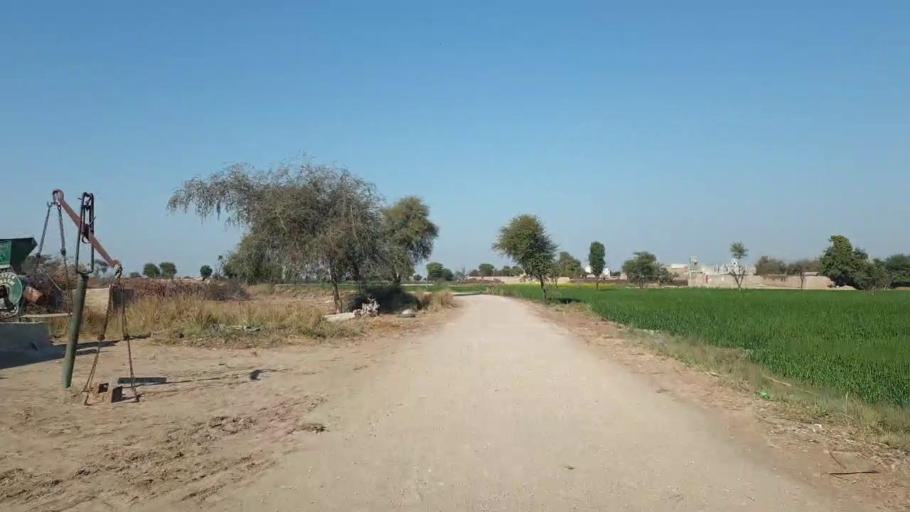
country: PK
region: Sindh
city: Shahdadpur
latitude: 25.9778
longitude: 68.6796
